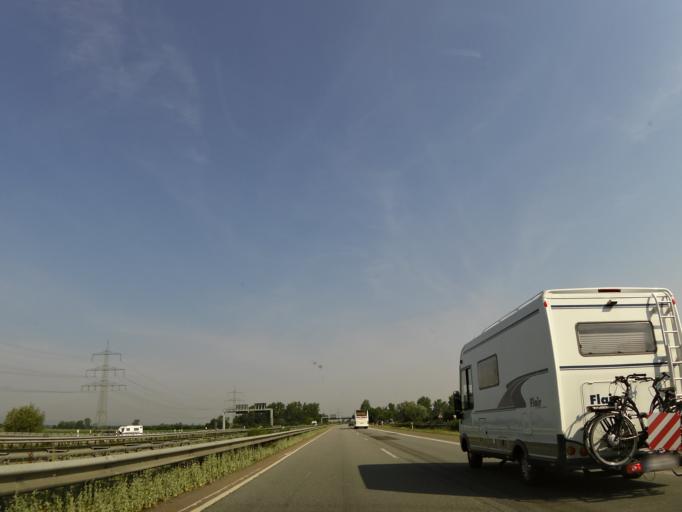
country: DE
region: Rheinland-Pfalz
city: Dannstadt-Schauernheim
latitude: 49.4435
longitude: 8.3235
